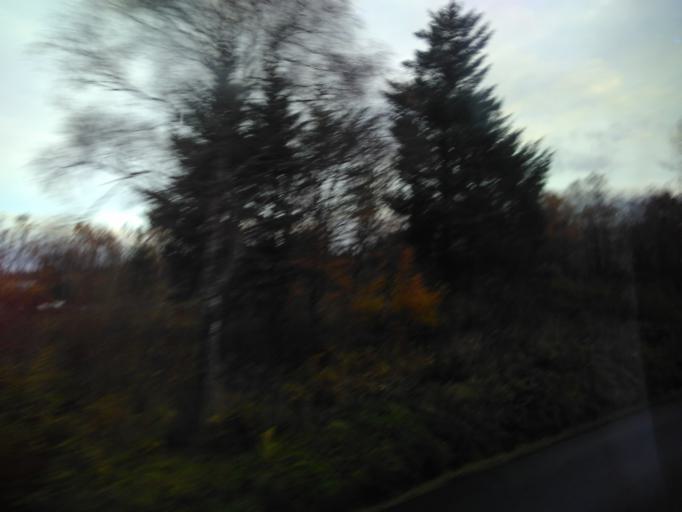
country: NO
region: Sor-Trondelag
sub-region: Froya
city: Sistranda
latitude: 63.6353
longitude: 8.8411
